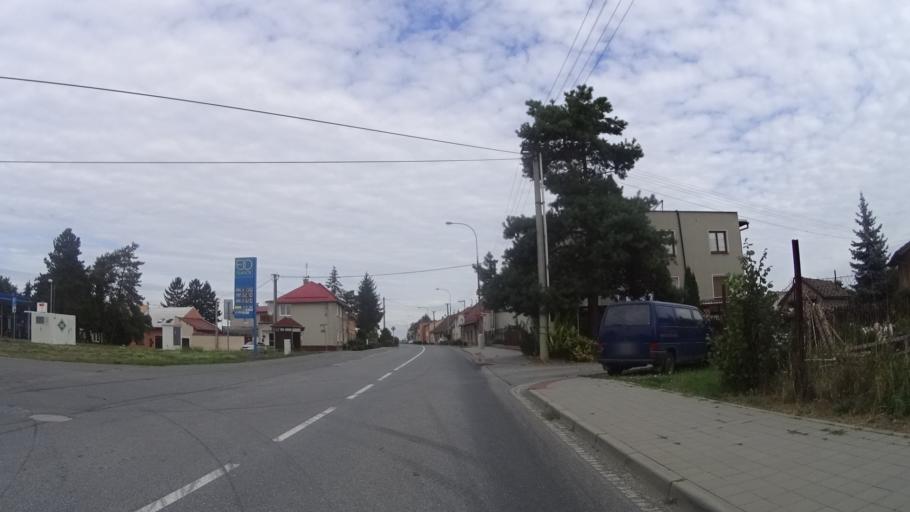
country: CZ
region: Olomoucky
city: Tovacov
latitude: 49.4369
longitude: 17.2845
